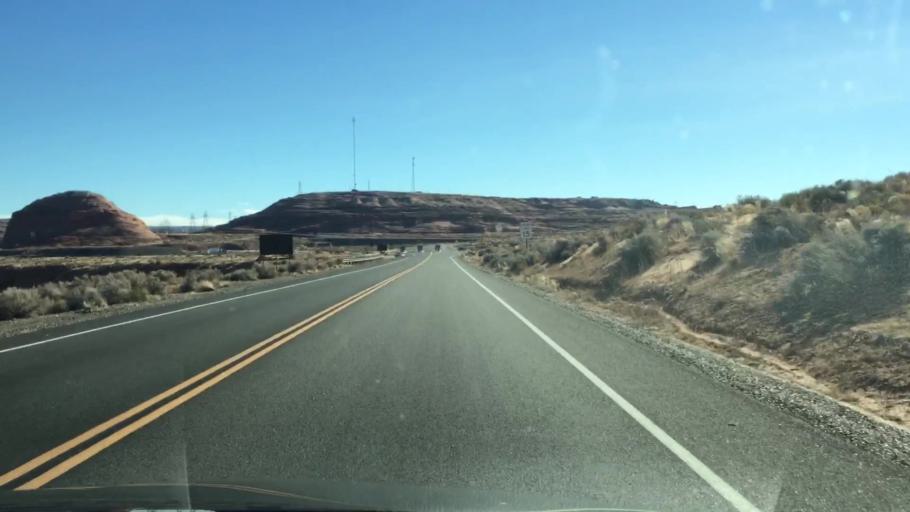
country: US
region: Arizona
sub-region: Coconino County
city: Page
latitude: 36.9458
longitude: -111.4937
